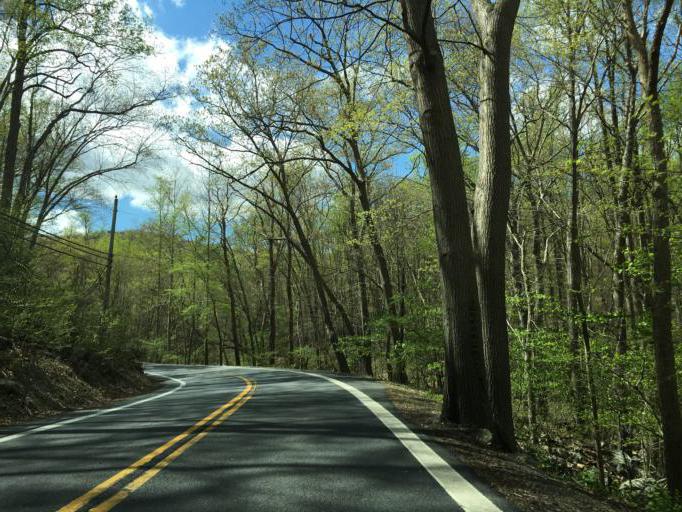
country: US
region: Maryland
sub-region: Frederick County
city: Thurmont
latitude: 39.6208
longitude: -77.4343
